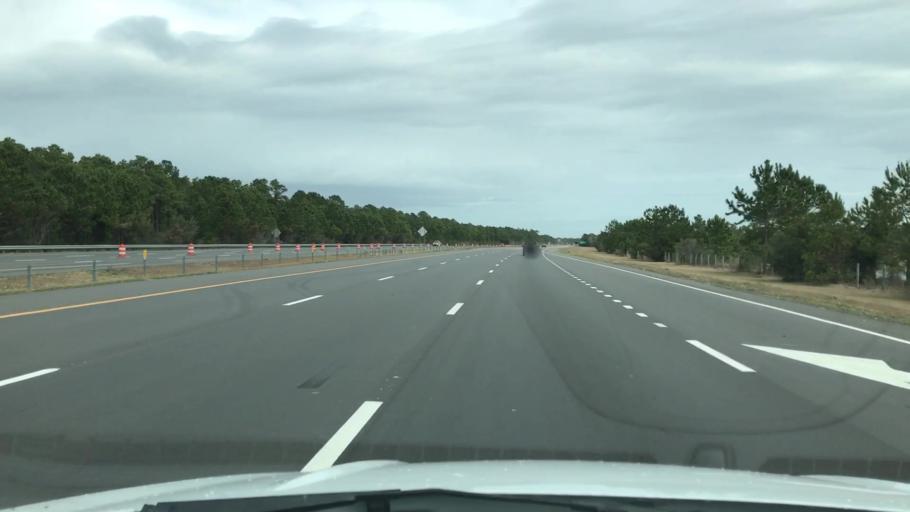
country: US
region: South Carolina
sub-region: Horry County
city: Socastee
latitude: 33.7105
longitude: -79.0079
